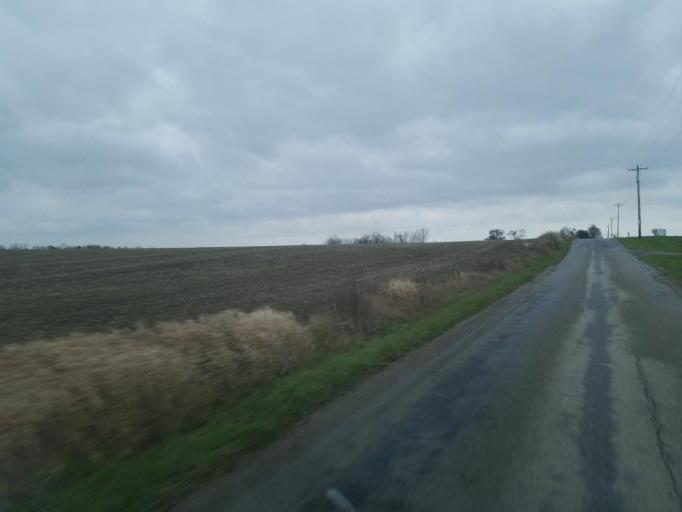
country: US
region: Ohio
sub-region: Morrow County
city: Mount Gilead
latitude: 40.5824
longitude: -82.7573
